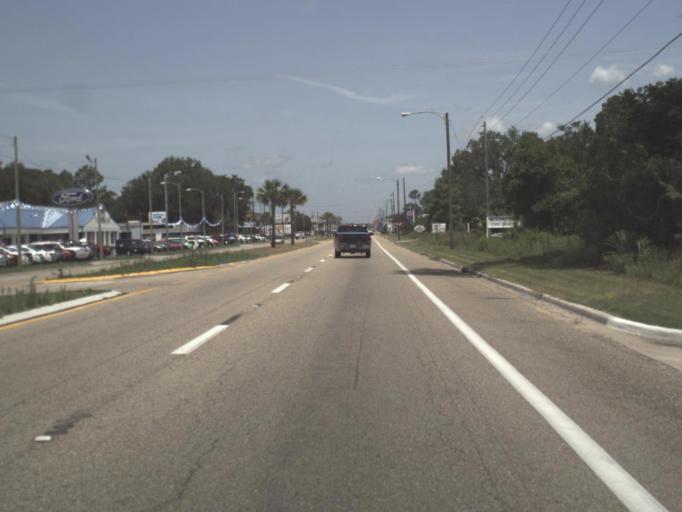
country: US
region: Florida
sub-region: Taylor County
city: Perry
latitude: 30.0890
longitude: -83.5736
